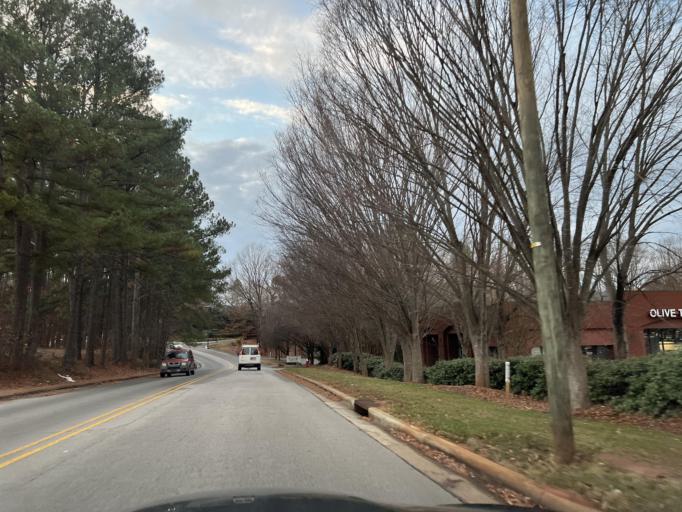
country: US
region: North Carolina
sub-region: Wake County
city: Cary
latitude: 35.7678
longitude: -78.7426
